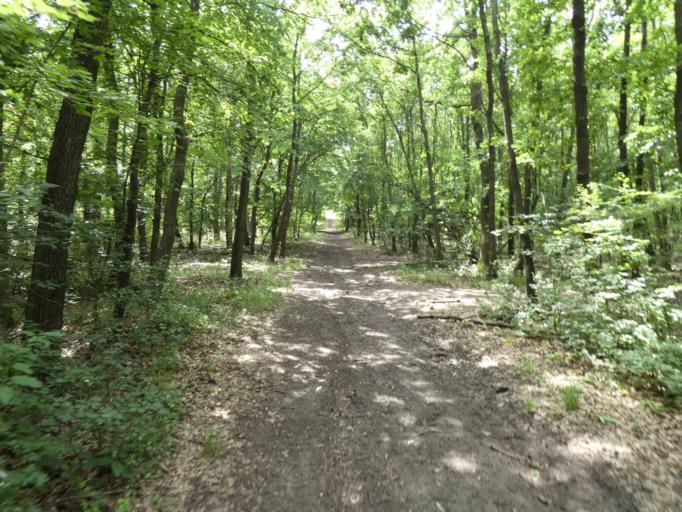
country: HU
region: Pest
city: Kismaros
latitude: 47.8426
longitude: 18.9665
